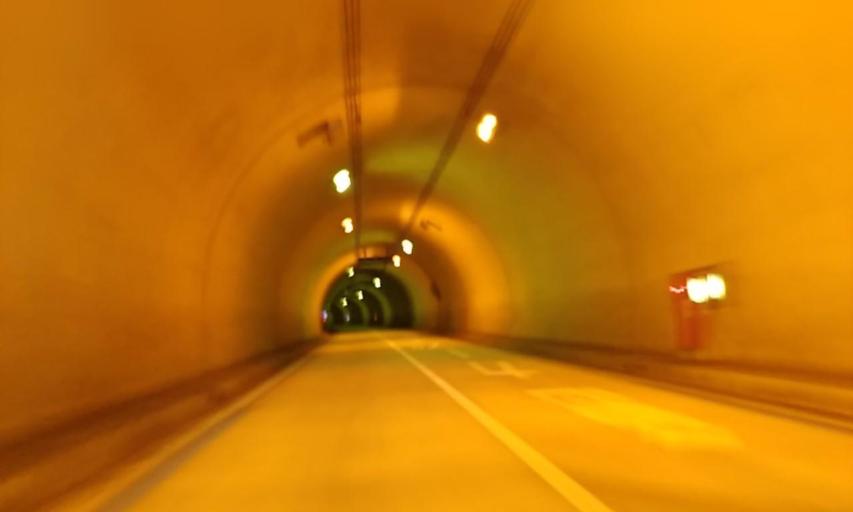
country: JP
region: Wakayama
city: Shingu
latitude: 33.8960
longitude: 135.8795
